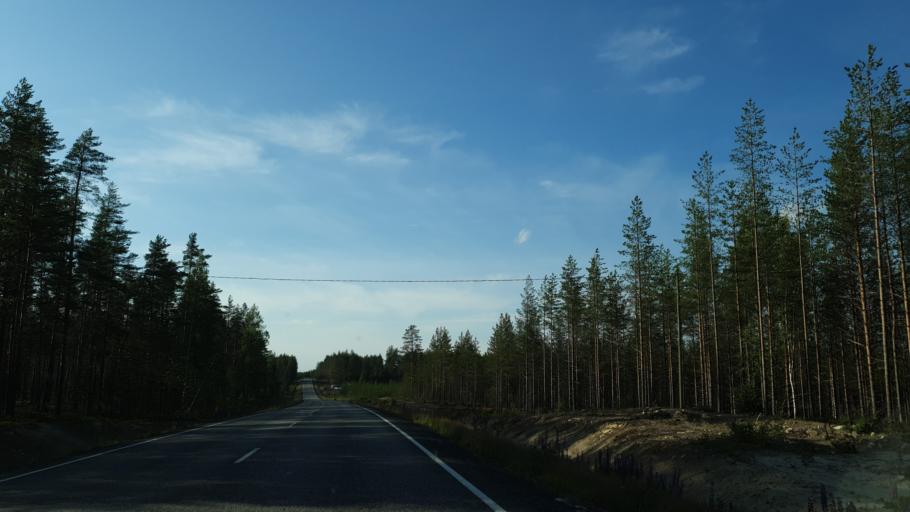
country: FI
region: Kainuu
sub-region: Kehys-Kainuu
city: Kuhmo
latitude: 64.0913
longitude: 29.4806
